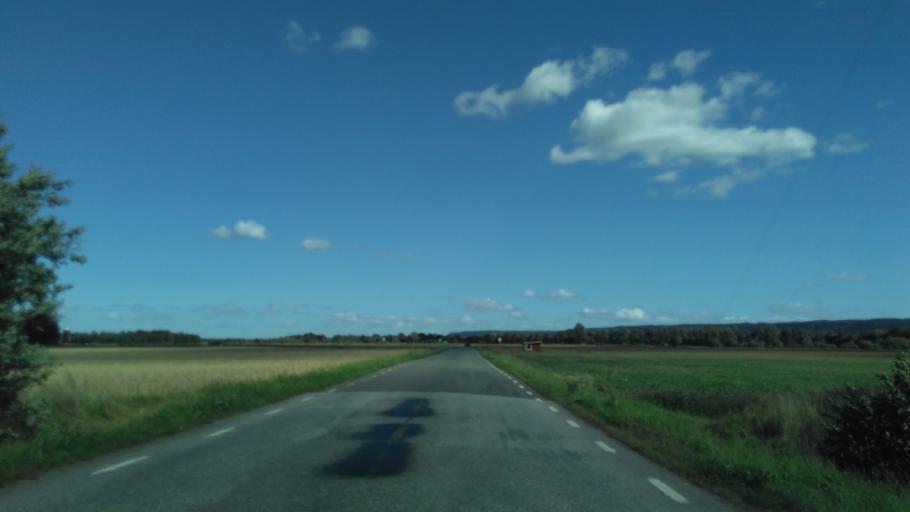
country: SE
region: Vaestra Goetaland
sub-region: Skara Kommun
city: Axvall
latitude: 58.4239
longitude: 13.6218
